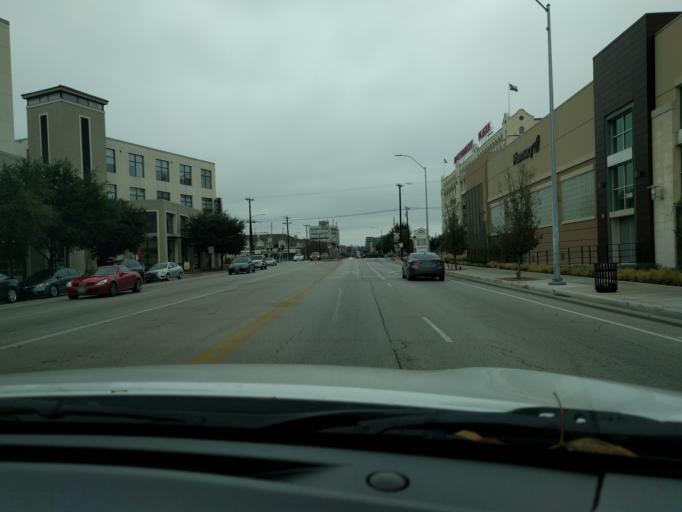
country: US
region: Texas
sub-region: Tarrant County
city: Fort Worth
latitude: 32.7511
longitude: -97.3513
